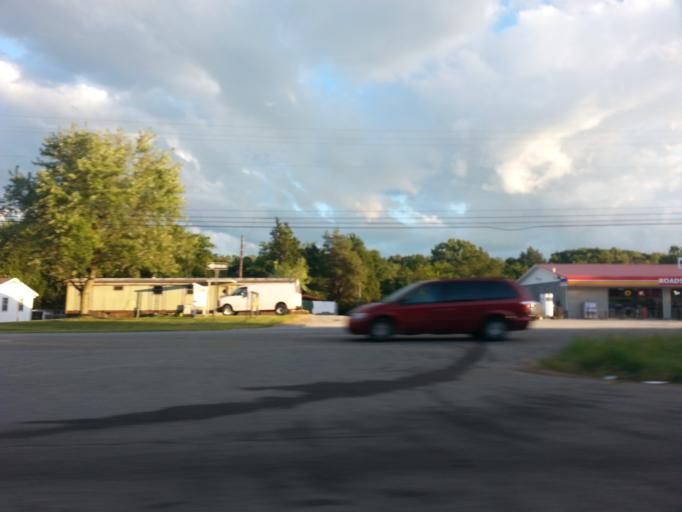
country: US
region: Tennessee
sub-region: Jefferson County
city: New Market
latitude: 36.0715
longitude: -83.6394
